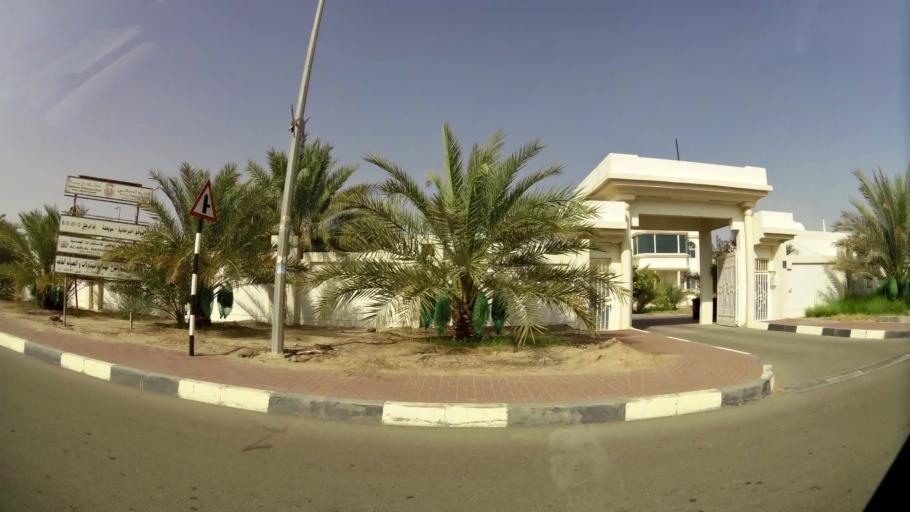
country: AE
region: Abu Dhabi
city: Al Ain
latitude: 24.2356
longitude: 55.6705
